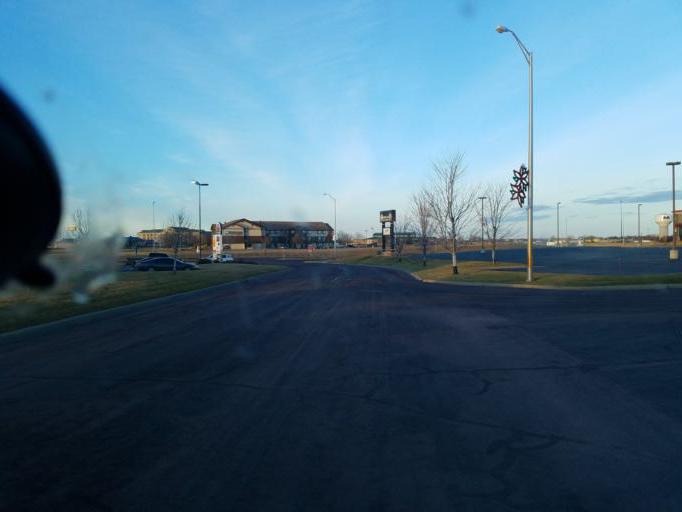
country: US
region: South Dakota
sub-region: Davison County
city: Mitchell
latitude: 43.6904
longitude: -98.0085
